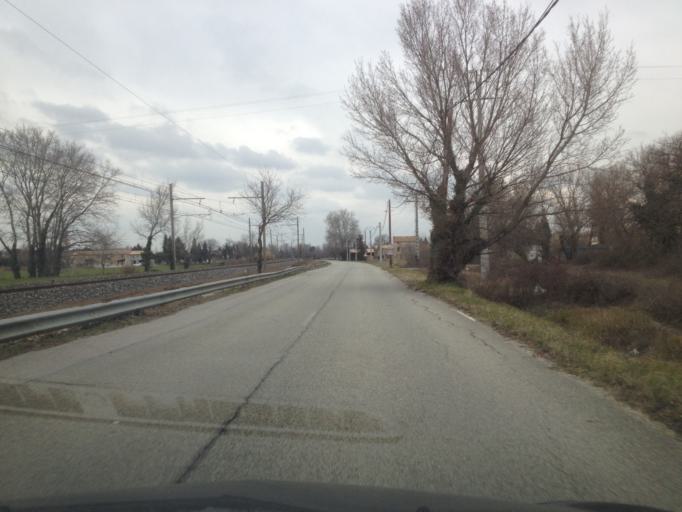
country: FR
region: Provence-Alpes-Cote d'Azur
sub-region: Departement du Vaucluse
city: Jonquieres
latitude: 44.1055
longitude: 4.8861
